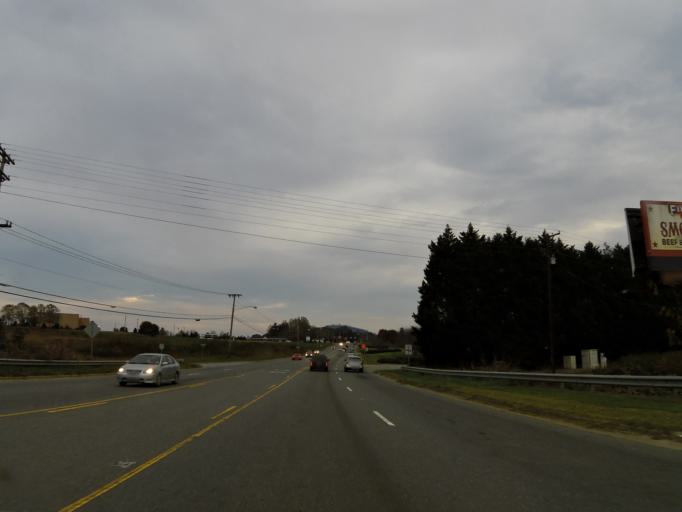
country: US
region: North Carolina
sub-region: Caldwell County
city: Lenoir
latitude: 35.9353
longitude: -81.5337
